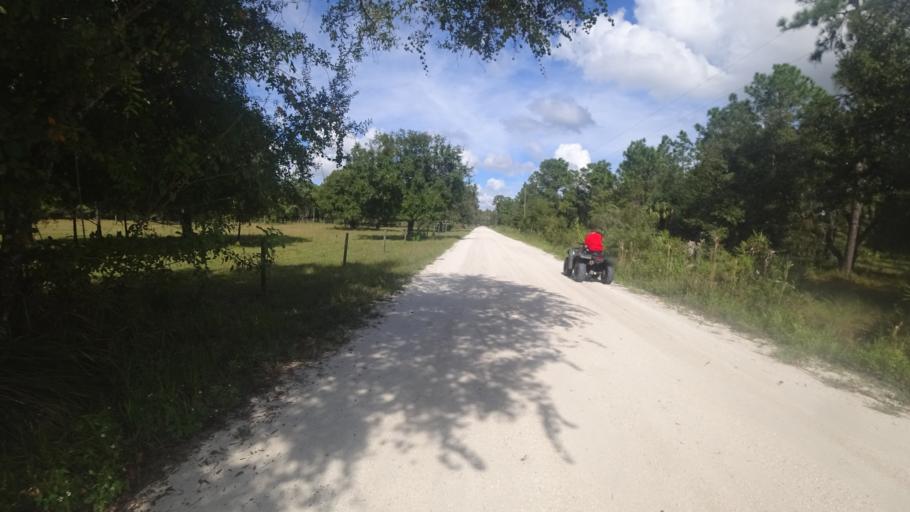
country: US
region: Florida
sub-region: Hillsborough County
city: Sun City Center
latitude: 27.6372
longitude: -82.3611
